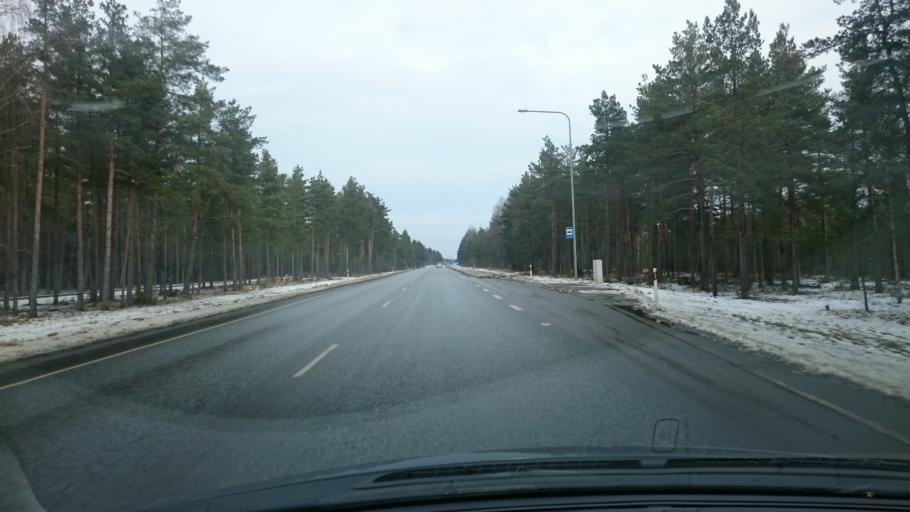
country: EE
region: Harju
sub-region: Saku vald
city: Saku
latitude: 59.3240
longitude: 24.6901
